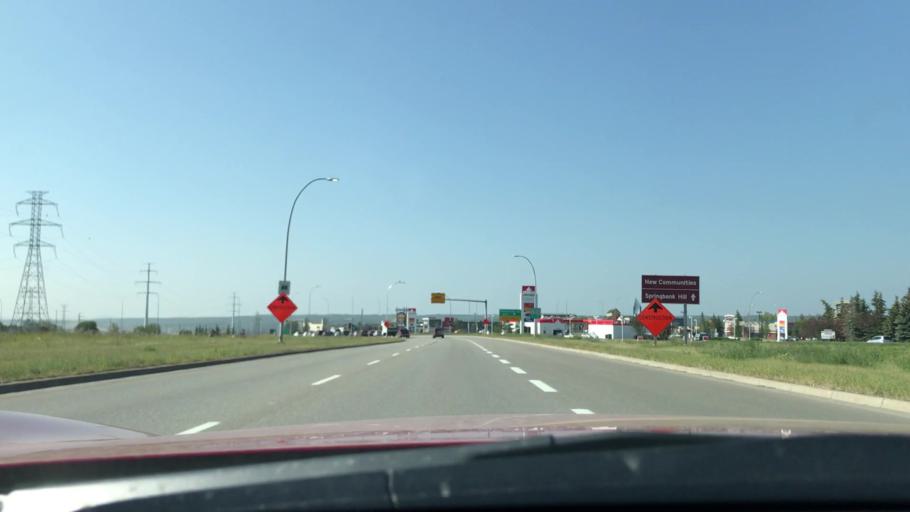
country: CA
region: Alberta
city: Calgary
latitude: 51.0209
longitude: -114.1653
